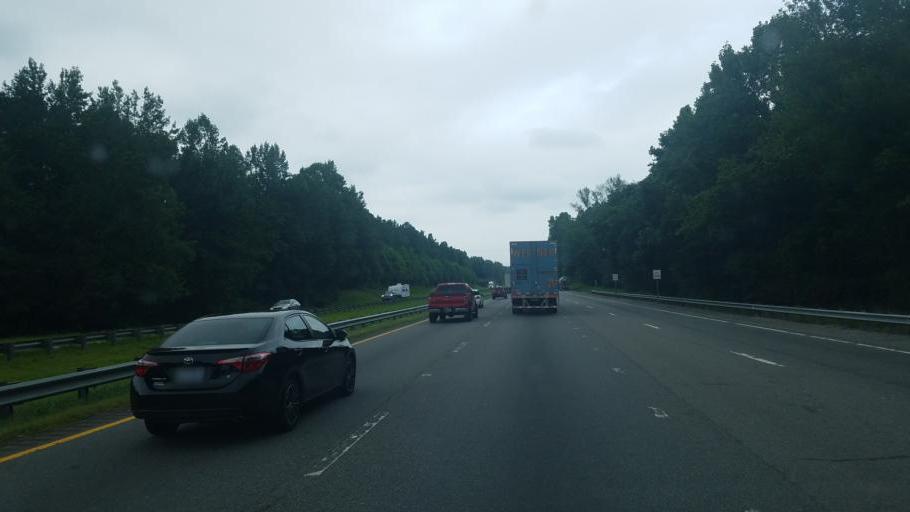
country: US
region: North Carolina
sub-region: Iredell County
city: Troutman
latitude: 35.6352
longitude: -80.8633
